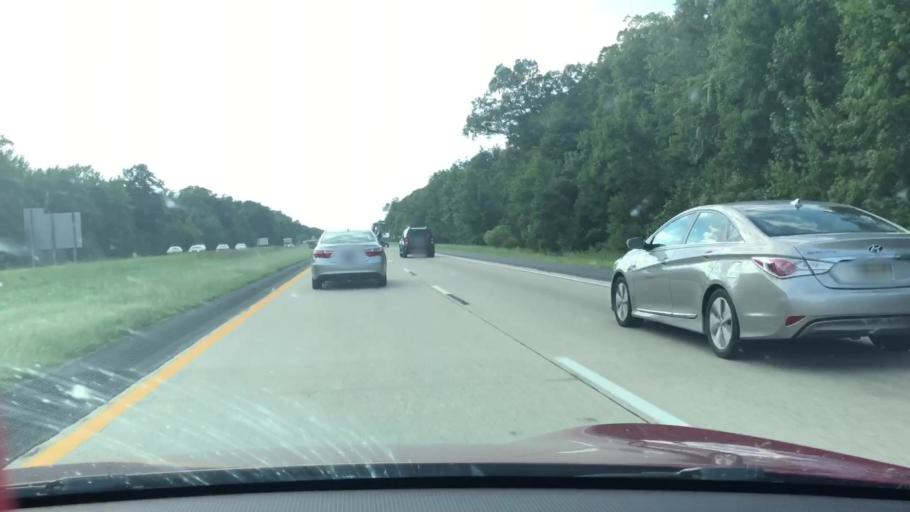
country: US
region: Delaware
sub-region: Kent County
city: Cheswold
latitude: 39.2175
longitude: -75.5581
